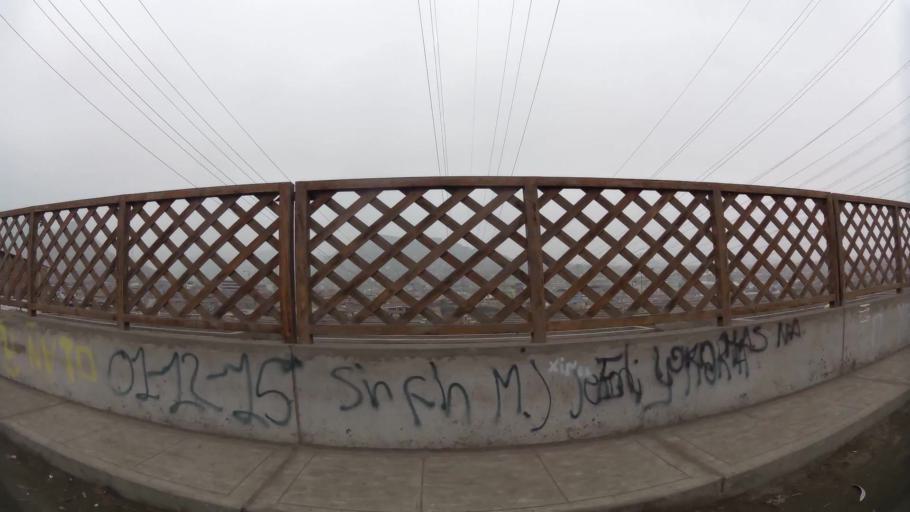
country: PE
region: Lima
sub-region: Lima
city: Surco
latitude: -12.1829
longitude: -76.9490
